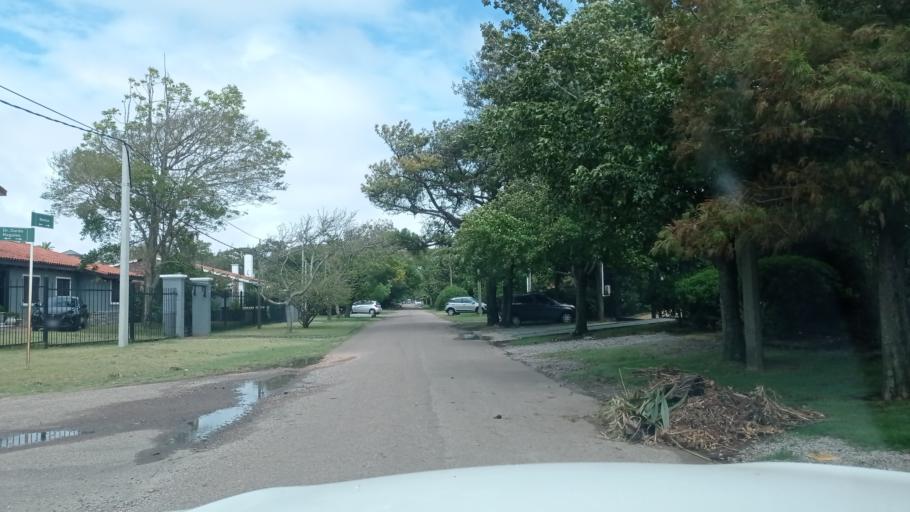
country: UY
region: Canelones
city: Barra de Carrasco
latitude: -34.8846
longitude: -56.0427
